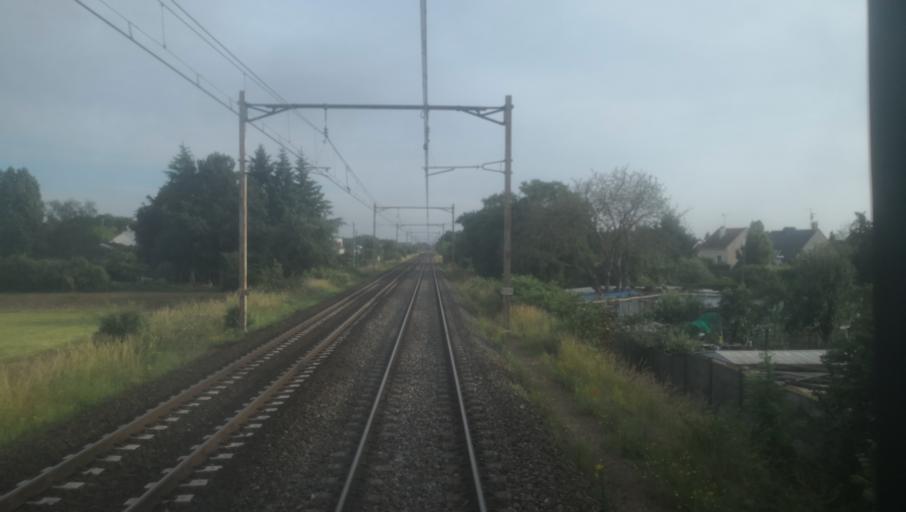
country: FR
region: Centre
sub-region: Departement du Loiret
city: Saint-Jean-le-Blanc
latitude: 47.8809
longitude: 1.9275
